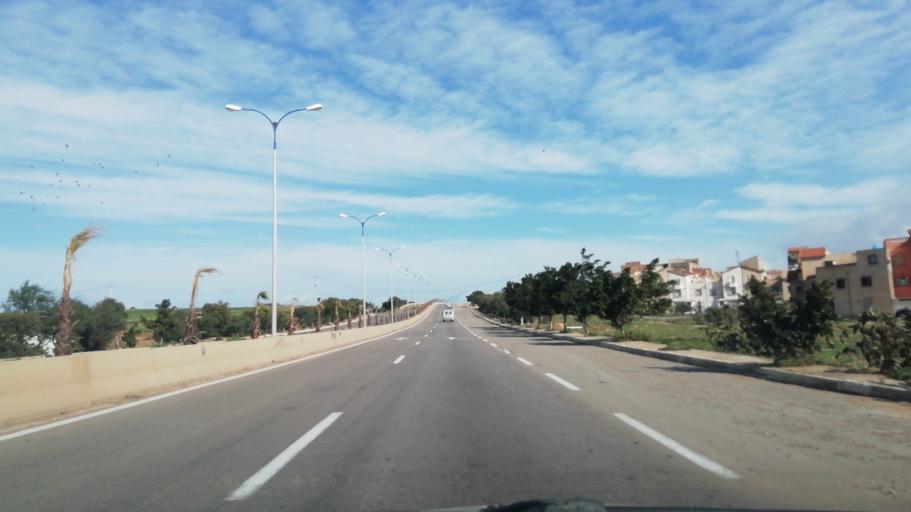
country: DZ
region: Mostaganem
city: Mostaganem
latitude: 35.8292
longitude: -0.0110
